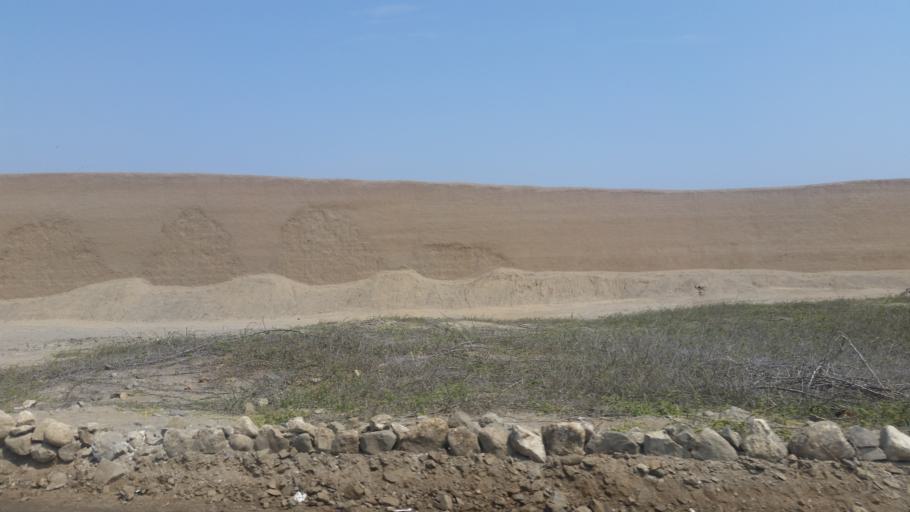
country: PE
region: La Libertad
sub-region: Provincia de Trujillo
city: La Esperanza
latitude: -8.1016
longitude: -79.0719
